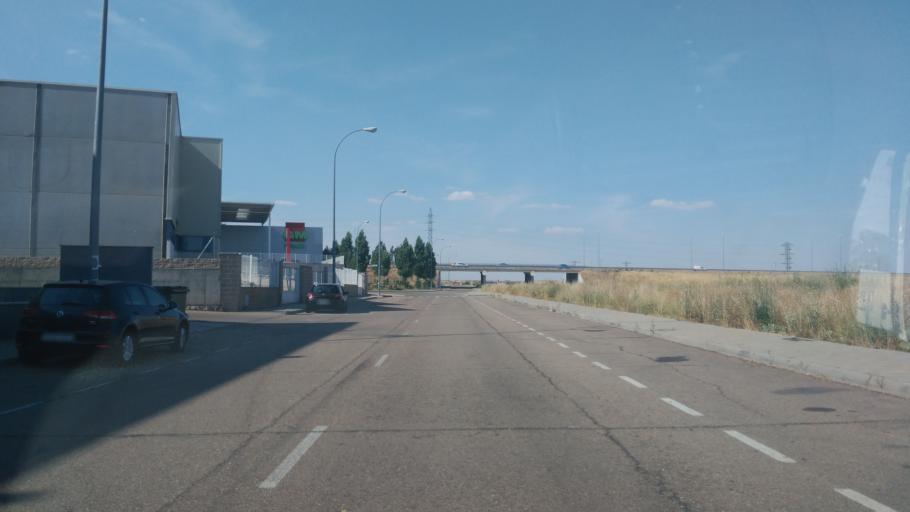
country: ES
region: Castille and Leon
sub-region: Provincia de Salamanca
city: Carbajosa de la Sagrada
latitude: 40.9406
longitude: -5.6519
